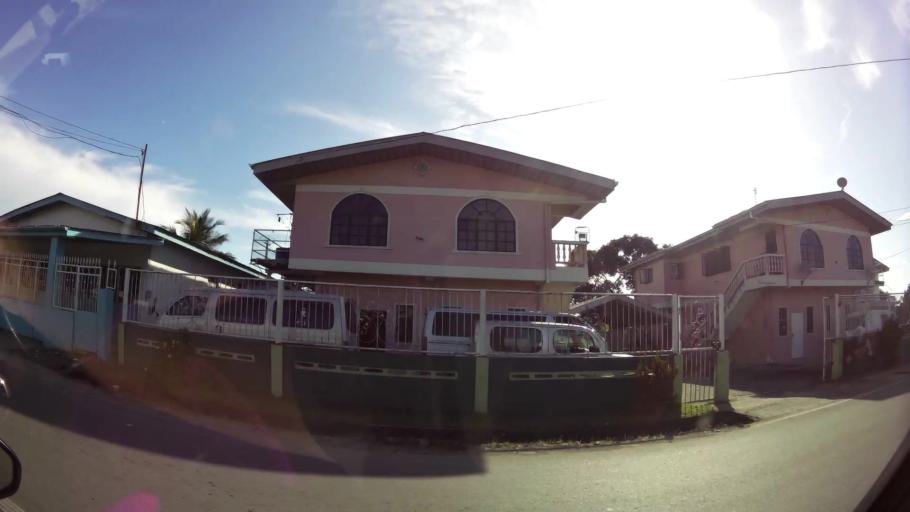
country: TT
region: Chaguanas
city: Chaguanas
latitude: 10.5304
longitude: -61.3789
